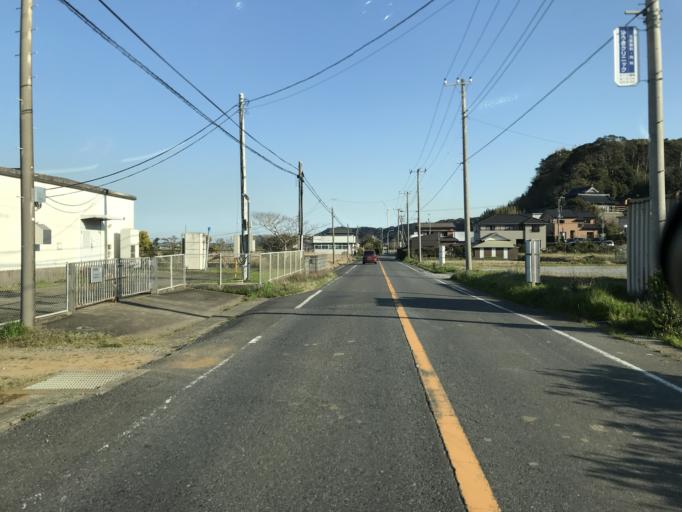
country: JP
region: Chiba
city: Asahi
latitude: 35.7355
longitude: 140.6962
